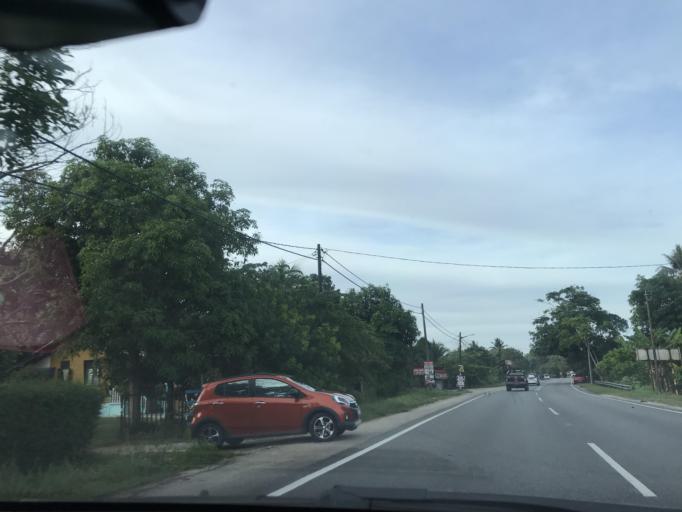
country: MY
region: Kelantan
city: Kota Bharu
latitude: 6.0940
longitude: 102.2086
